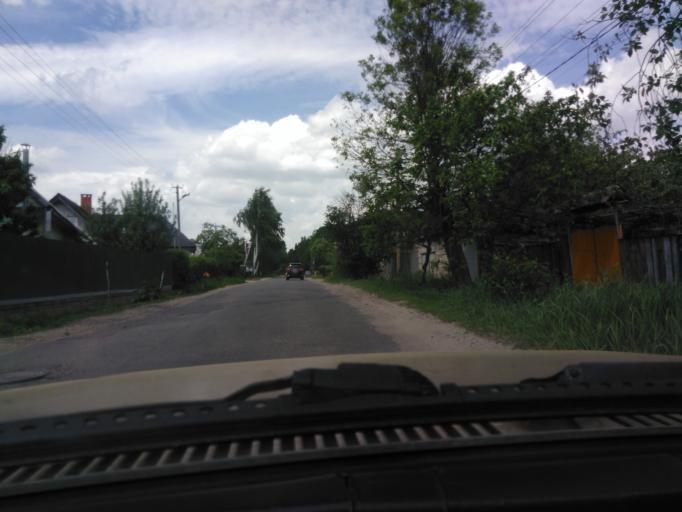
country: BY
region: Mogilev
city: Mahilyow
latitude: 53.9339
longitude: 30.3213
